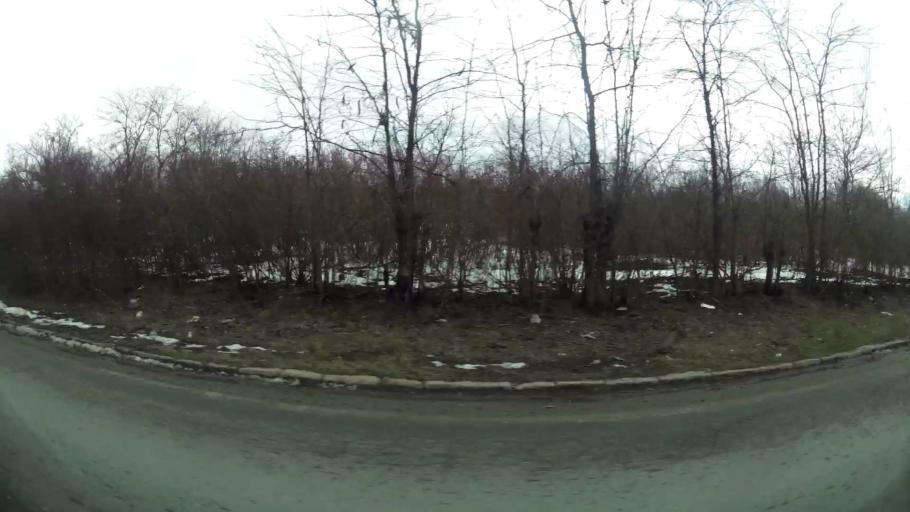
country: RS
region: Central Serbia
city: Sremcica
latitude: 44.7240
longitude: 20.3961
